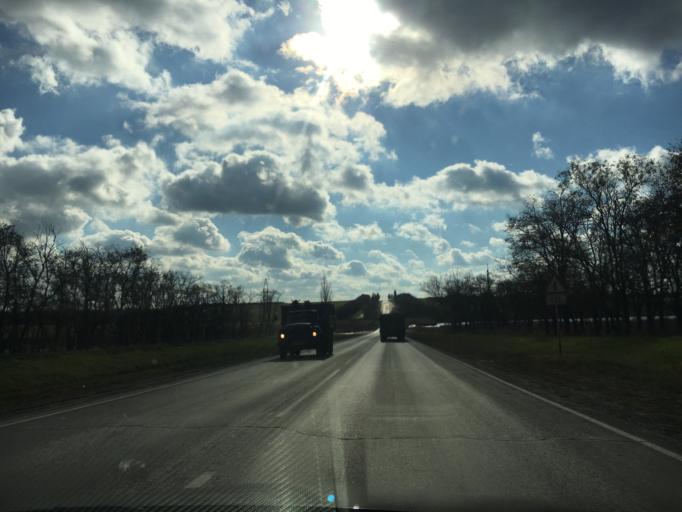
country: RU
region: Rostov
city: Matveyev Kurgan
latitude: 47.5519
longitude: 38.8903
